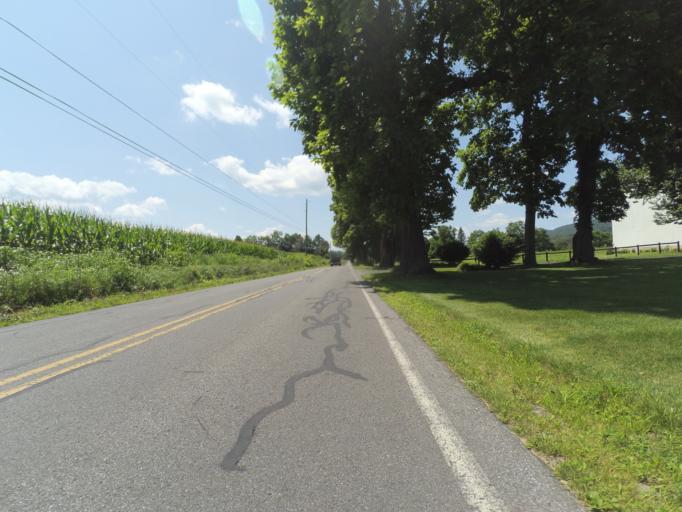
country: US
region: Pennsylvania
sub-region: Centre County
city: Centre Hall
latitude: 40.8227
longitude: -77.7253
